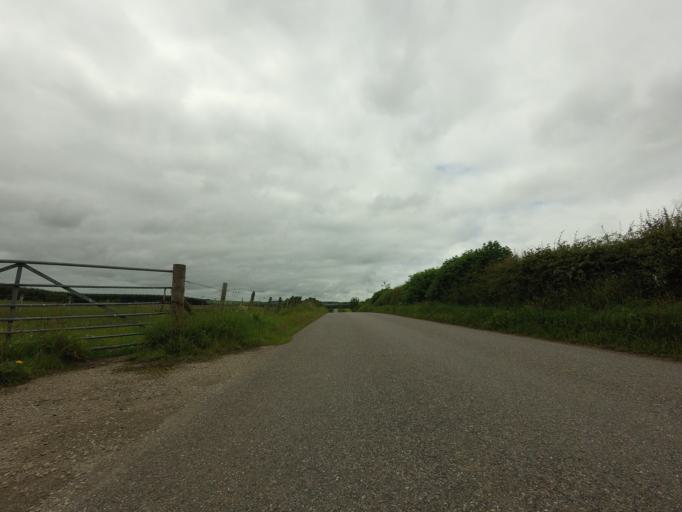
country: GB
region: Scotland
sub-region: Aberdeenshire
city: Mintlaw
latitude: 57.5249
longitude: -2.1398
